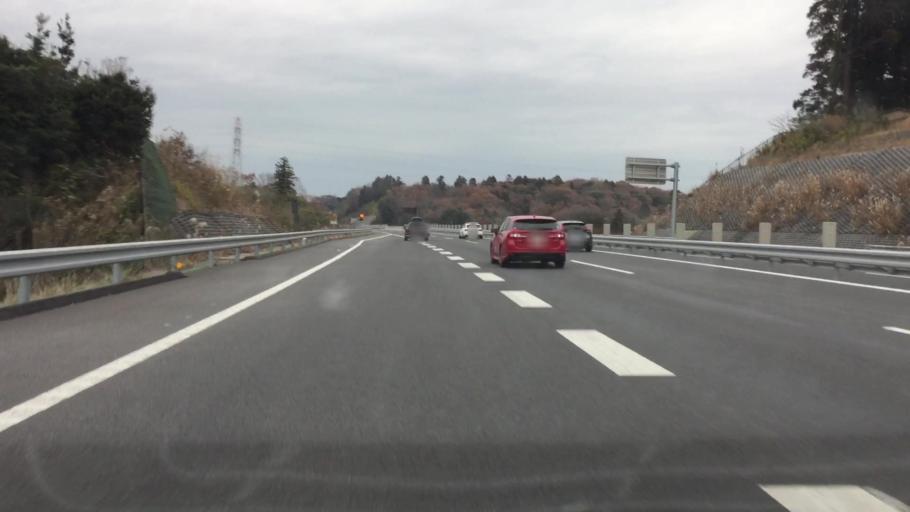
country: JP
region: Chiba
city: Sawara
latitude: 35.8648
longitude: 140.3915
